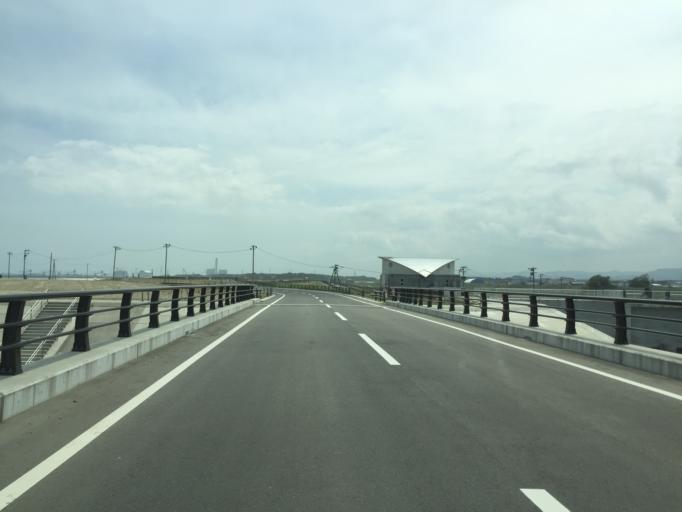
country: JP
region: Miyagi
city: Watari
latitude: 37.8921
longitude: 140.9298
